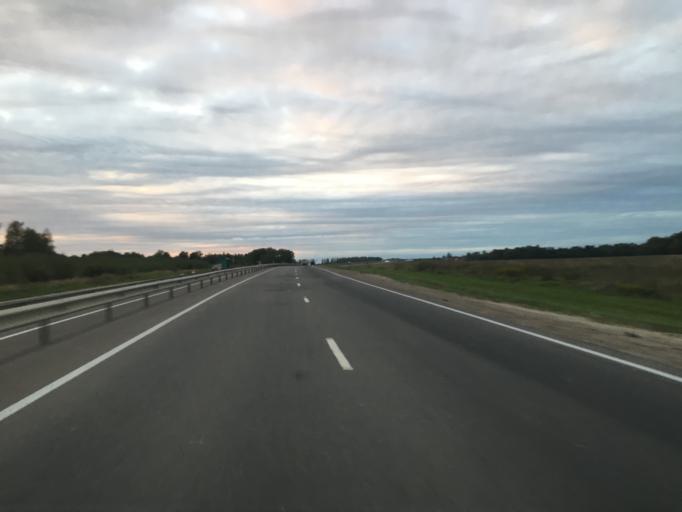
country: RU
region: Kaluga
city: Kaluga
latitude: 54.6131
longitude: 36.3040
